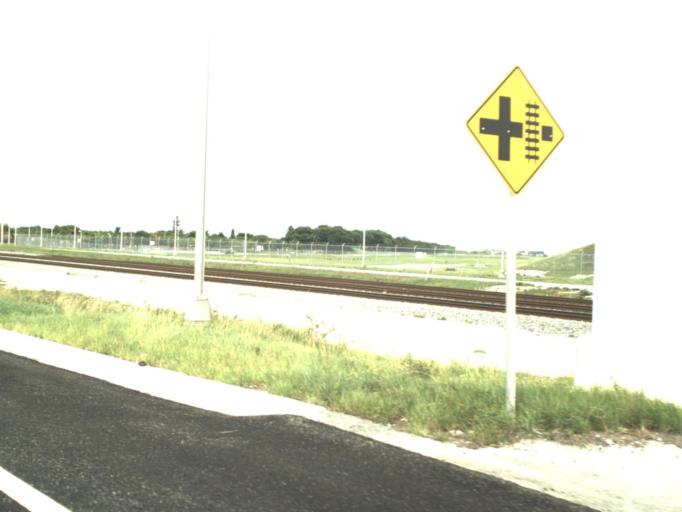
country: US
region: Florida
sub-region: Broward County
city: Dania Beach
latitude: 26.0649
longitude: -80.1412
